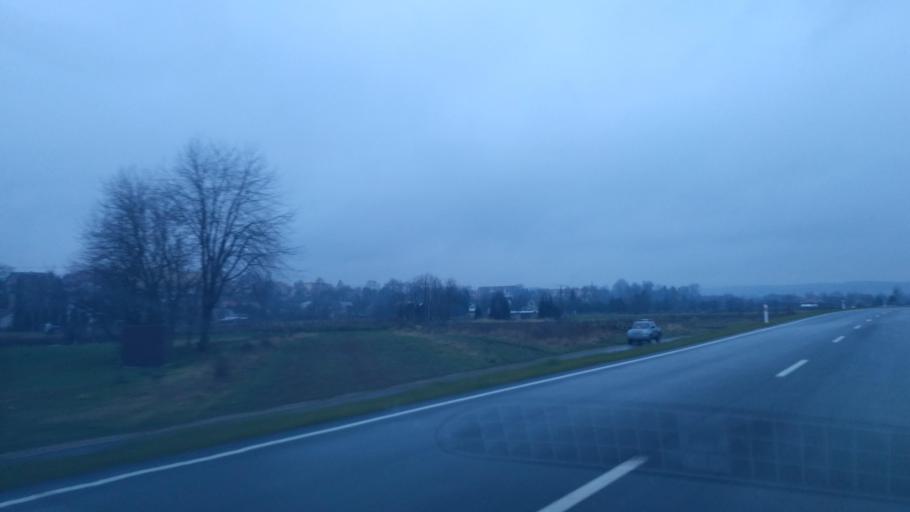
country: PL
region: Subcarpathian Voivodeship
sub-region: Powiat rzeszowski
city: Dynow
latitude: 49.8110
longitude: 22.2405
